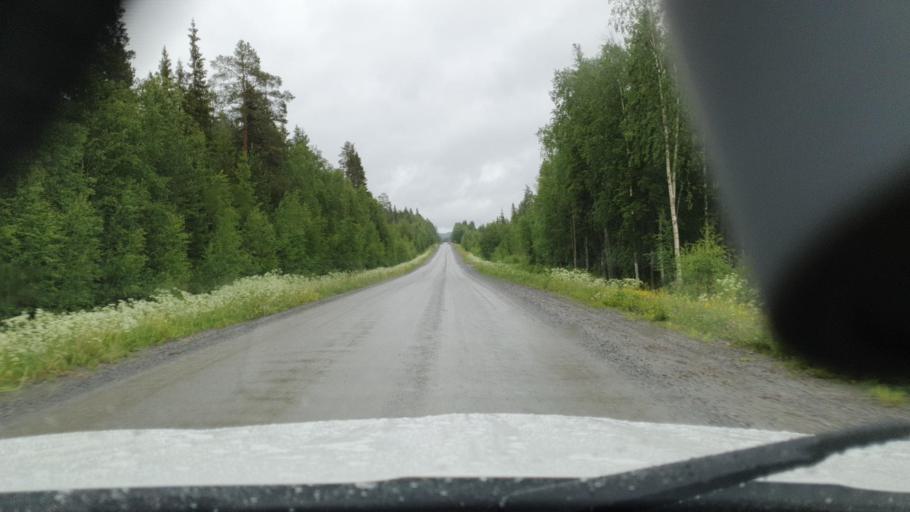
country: SE
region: Vaesterbotten
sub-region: Skelleftea Kommun
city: Burtraesk
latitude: 64.3779
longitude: 20.3499
